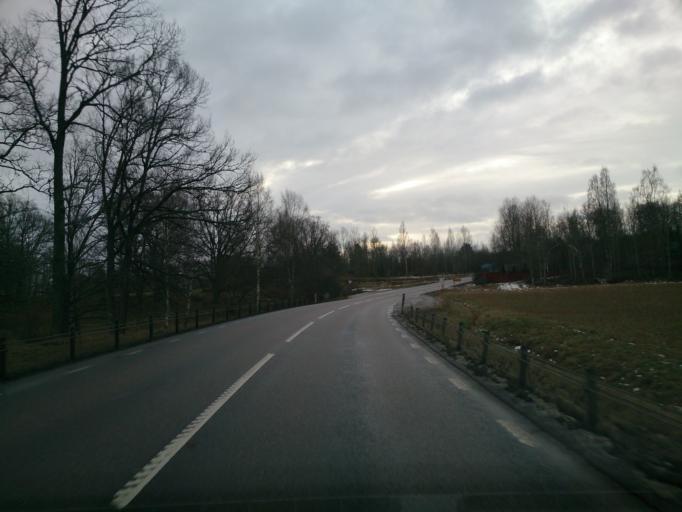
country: SE
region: OEstergoetland
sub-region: Atvidabergs Kommun
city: Atvidaberg
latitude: 58.2545
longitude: 15.9300
